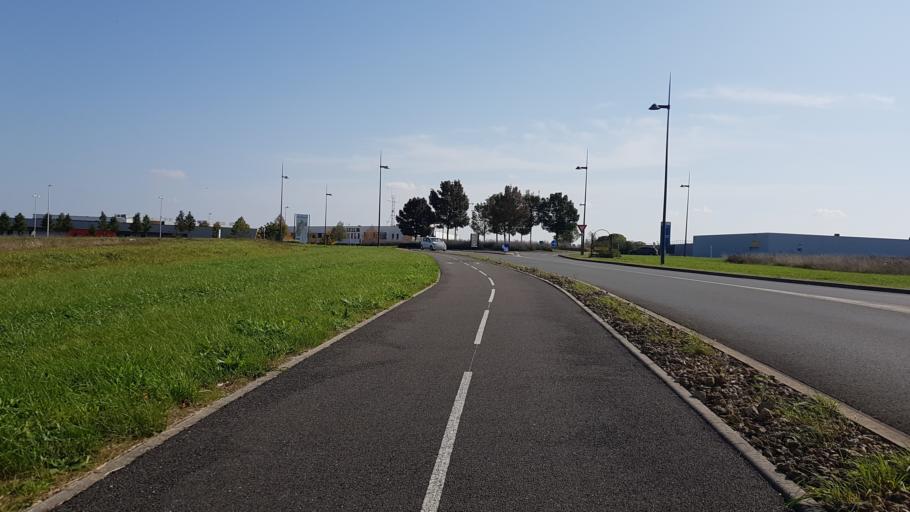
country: FR
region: Poitou-Charentes
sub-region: Departement de la Vienne
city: Chasseneuil-du-Poitou
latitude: 46.6554
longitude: 0.3611
